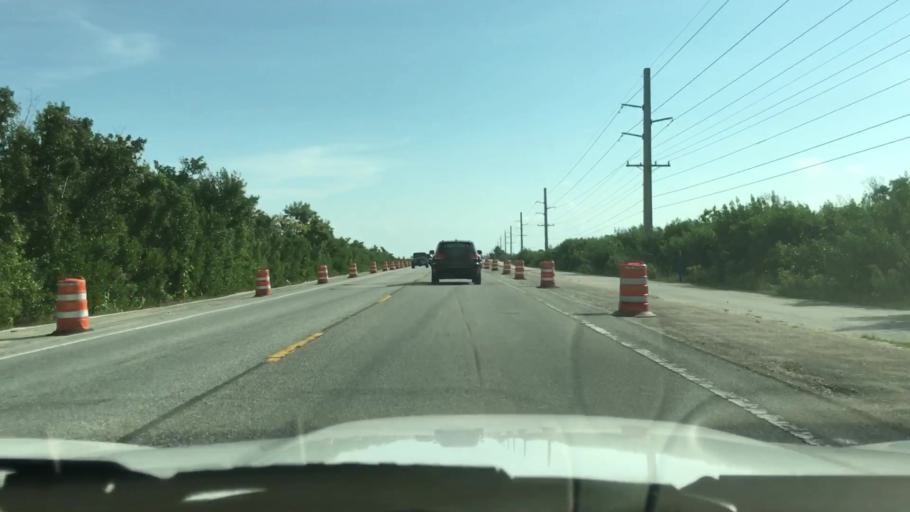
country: US
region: Florida
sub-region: Monroe County
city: Cudjoe Key
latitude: 24.6630
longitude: -81.4717
